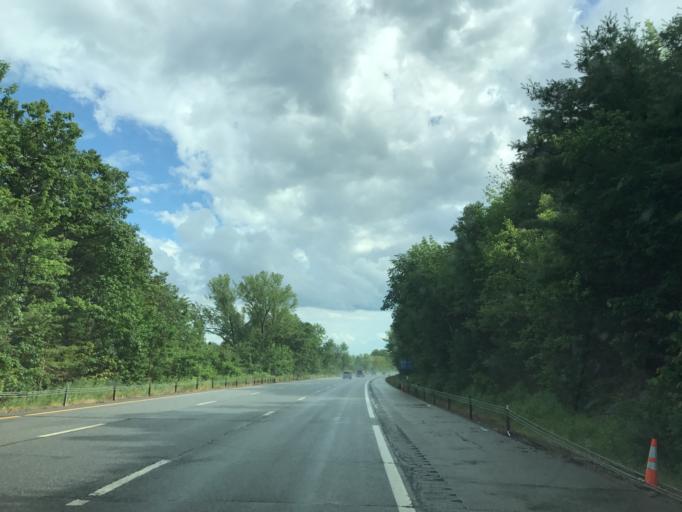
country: US
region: New York
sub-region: Warren County
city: Glens Falls North
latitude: 43.3731
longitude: -73.7015
